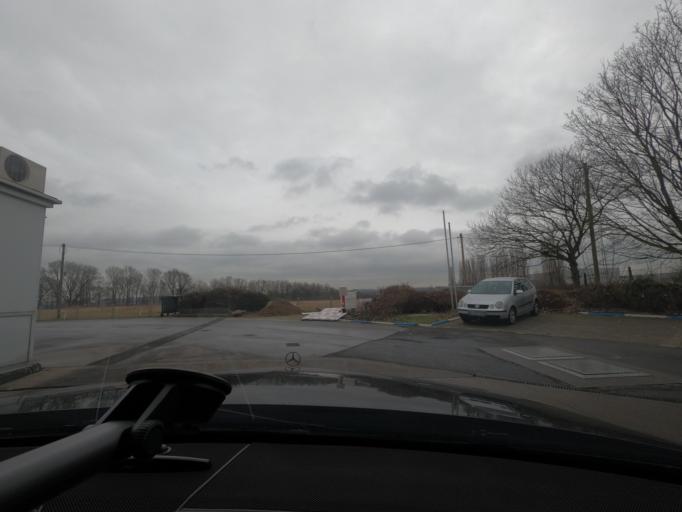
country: DE
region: North Rhine-Westphalia
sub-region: Regierungsbezirk Arnsberg
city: Holzwickede
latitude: 51.5051
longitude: 7.5735
